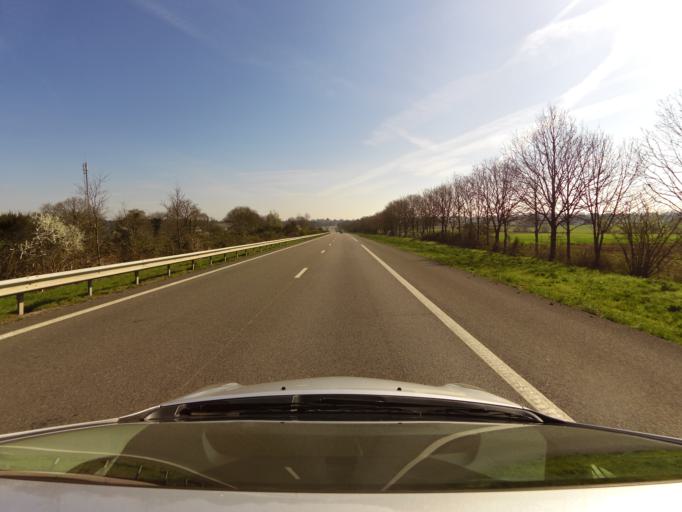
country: FR
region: Brittany
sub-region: Departement d'Ille-et-Vilaine
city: Saint-Thurial
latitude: 48.0419
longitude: -1.9477
